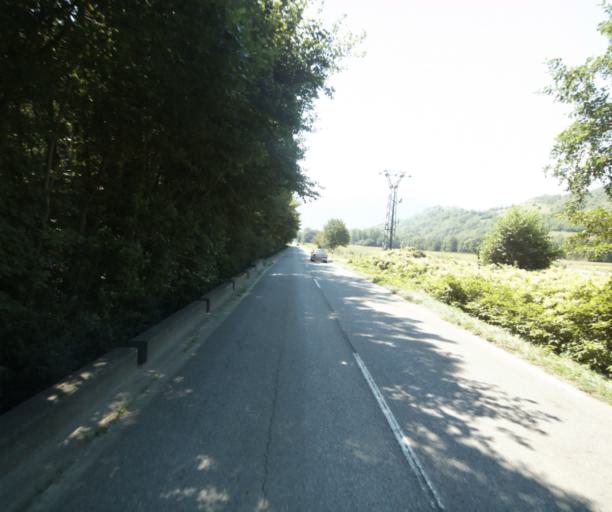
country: FR
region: Rhone-Alpes
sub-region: Departement de l'Isere
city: Vaulnaveys-le-Haut
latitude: 45.1034
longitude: 5.7991
